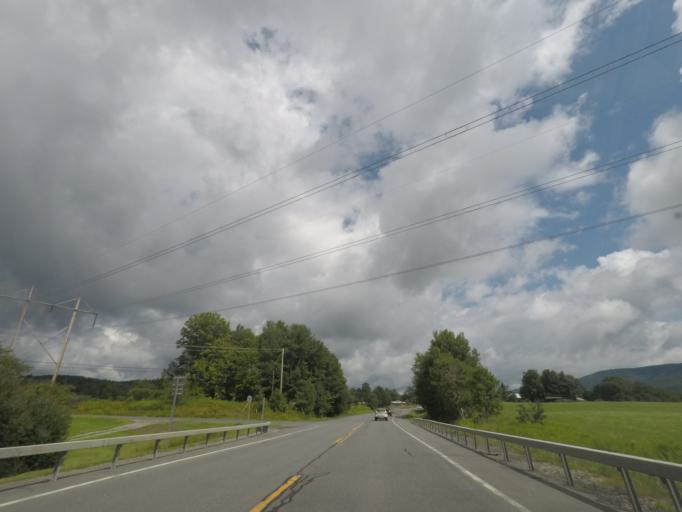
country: US
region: Massachusetts
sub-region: Berkshire County
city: Lanesborough
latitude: 42.5567
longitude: -73.3743
